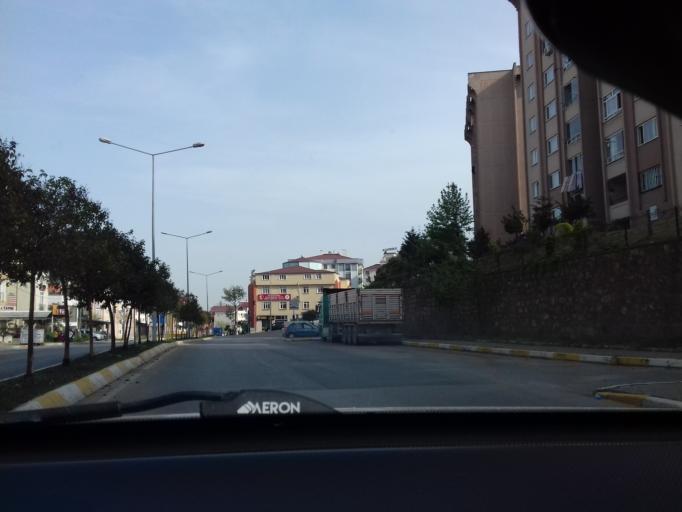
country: TR
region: Istanbul
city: Pendik
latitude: 40.9103
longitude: 29.2794
